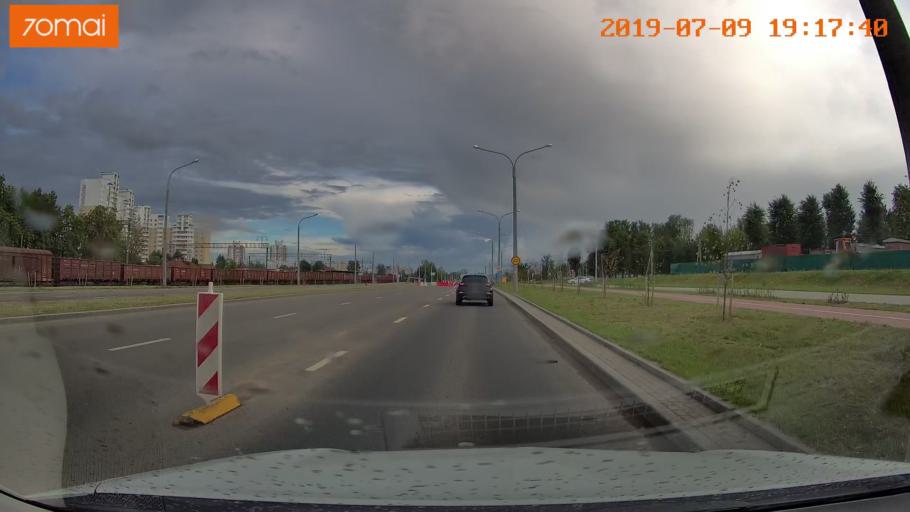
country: BY
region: Minsk
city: Minsk
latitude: 53.8677
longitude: 27.5606
